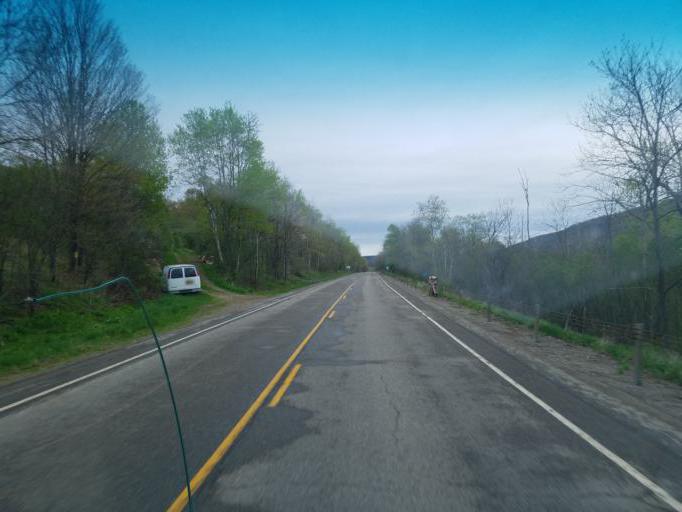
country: US
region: New York
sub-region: Allegany County
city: Andover
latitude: 42.0099
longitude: -77.8423
